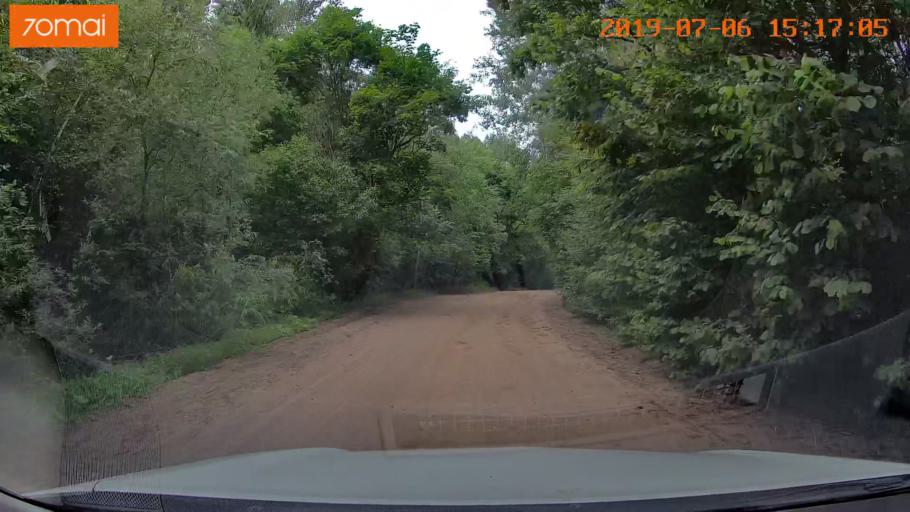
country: BY
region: Minsk
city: Ivyanyets
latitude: 53.9857
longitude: 26.6701
